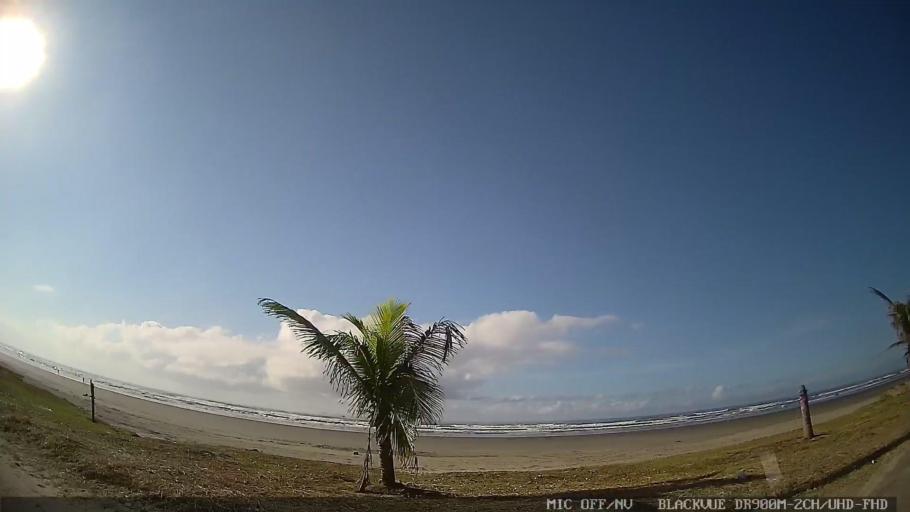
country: BR
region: Sao Paulo
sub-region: Peruibe
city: Peruibe
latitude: -24.2760
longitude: -46.9365
